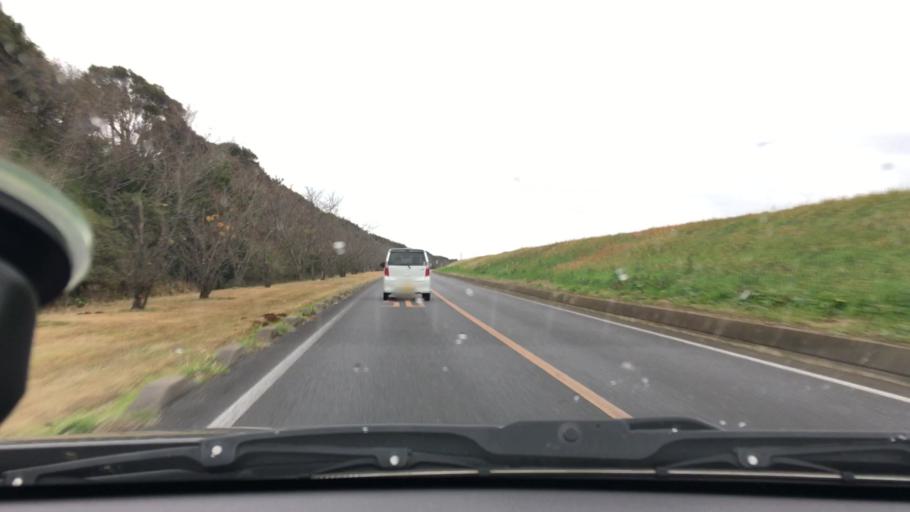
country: JP
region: Chiba
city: Omigawa
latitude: 35.8520
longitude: 140.6814
